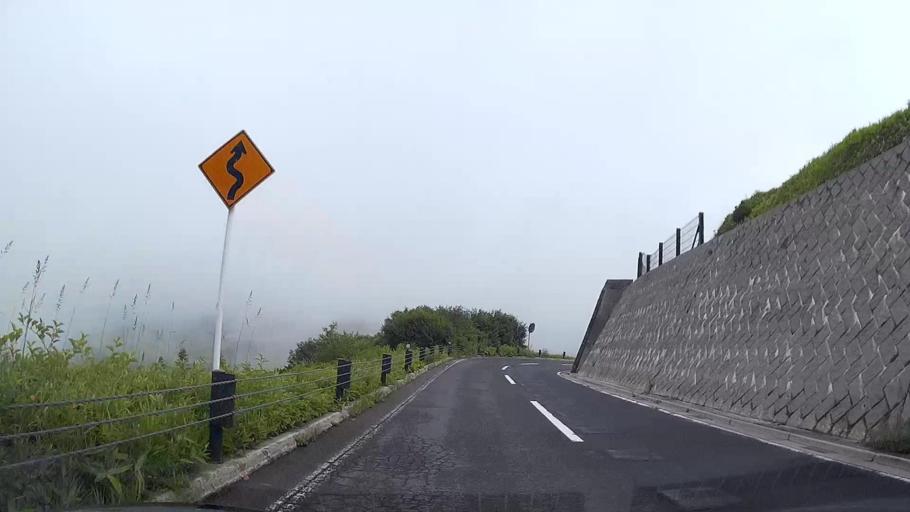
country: JP
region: Nagano
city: Nakano
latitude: 36.6558
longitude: 138.5300
